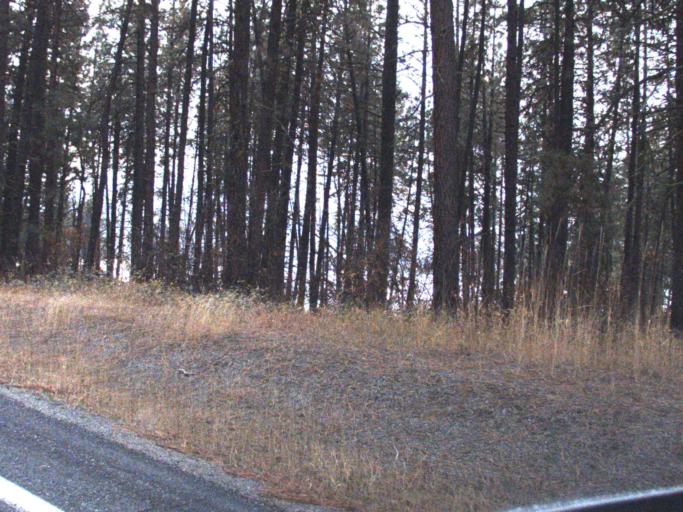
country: US
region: Washington
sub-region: Stevens County
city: Kettle Falls
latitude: 48.3047
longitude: -118.1491
